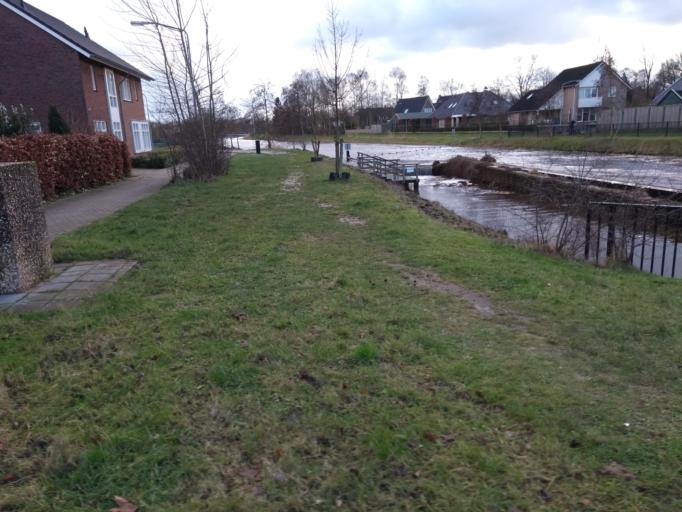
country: NL
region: Overijssel
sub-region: Gemeente Almelo
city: Almelo
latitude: 52.3745
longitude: 6.6956
